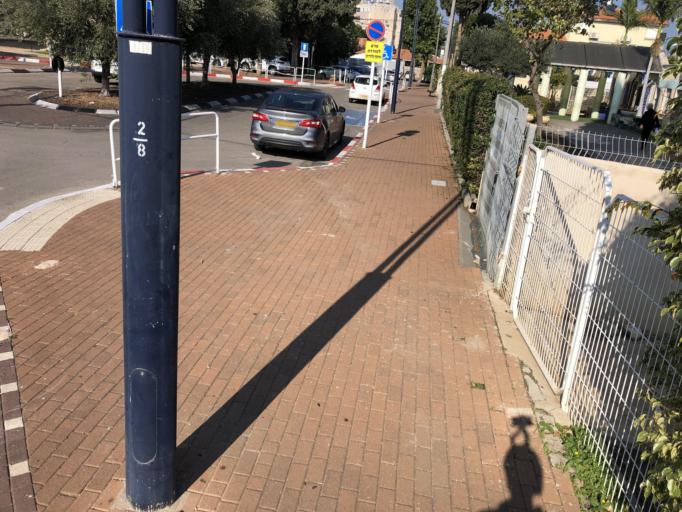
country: IL
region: Northern District
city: `Akko
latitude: 32.9262
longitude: 35.0928
